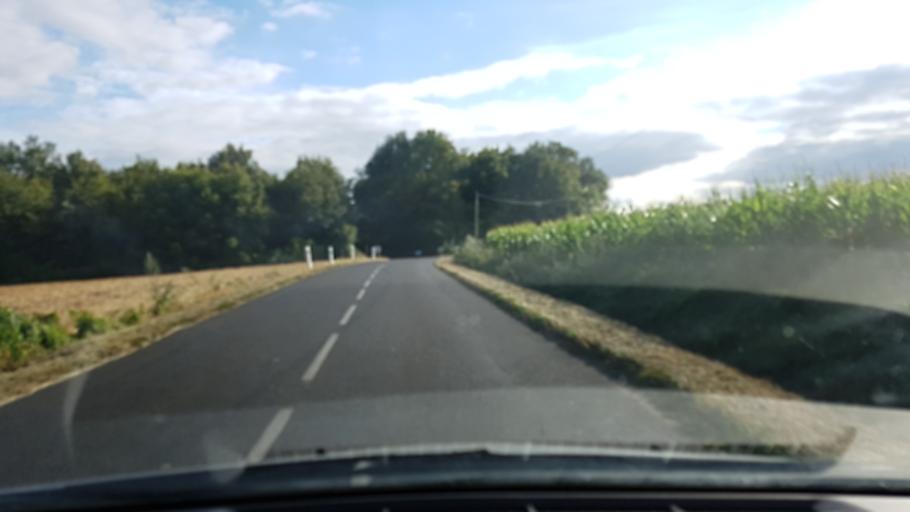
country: FR
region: Pays de la Loire
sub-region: Departement de Maine-et-Loire
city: Maze
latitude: 47.4916
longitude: -0.2747
